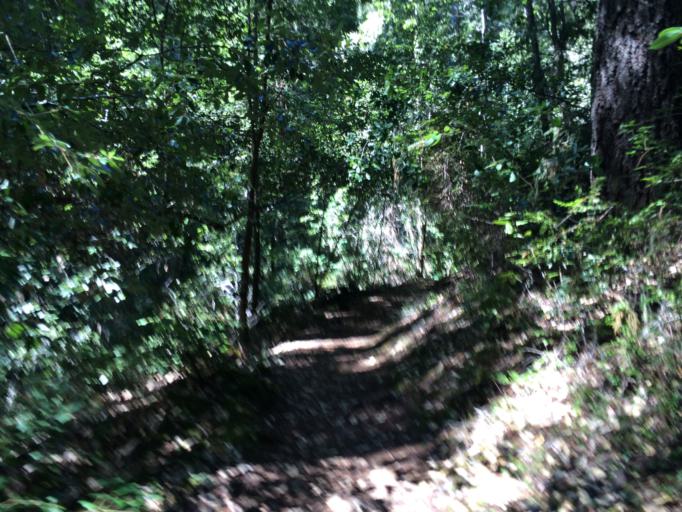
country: US
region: California
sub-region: Santa Cruz County
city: Boulder Creek
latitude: 37.1847
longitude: -122.2183
